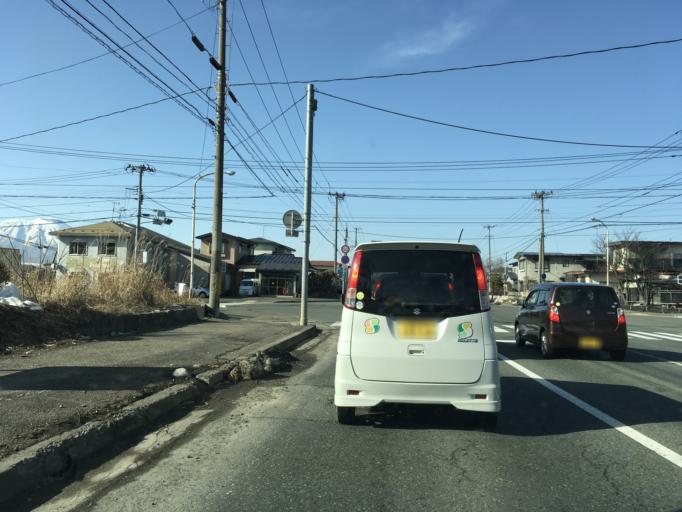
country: JP
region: Iwate
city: Morioka-shi
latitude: 39.7474
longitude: 141.1673
